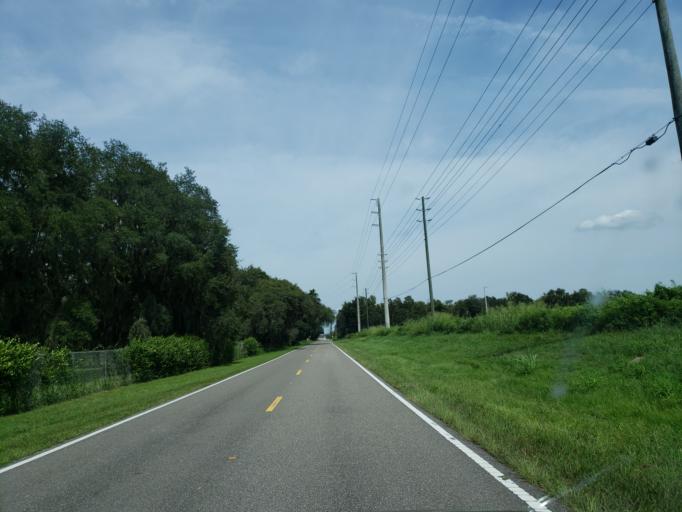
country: US
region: Florida
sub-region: Pasco County
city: Wesley Chapel
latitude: 28.2780
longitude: -82.3079
